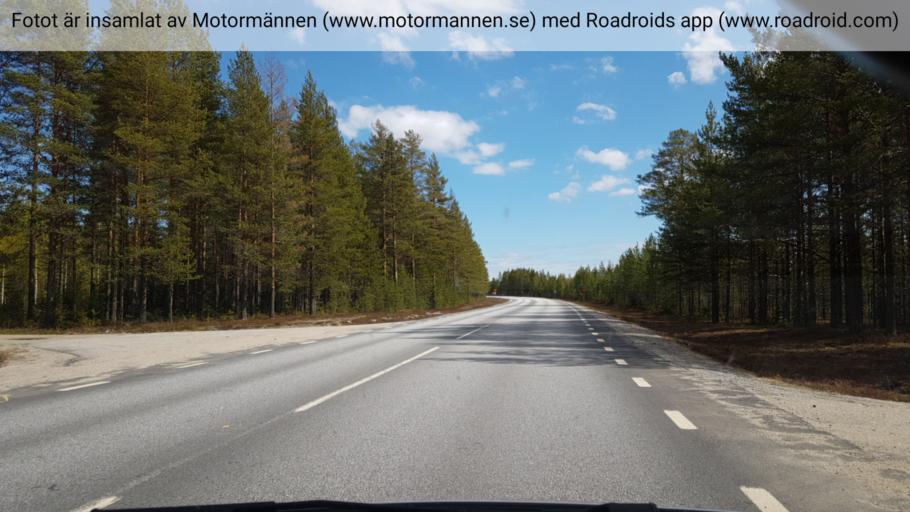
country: SE
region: Vaesterbotten
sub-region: Vindelns Kommun
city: Vindeln
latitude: 64.1650
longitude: 19.8081
